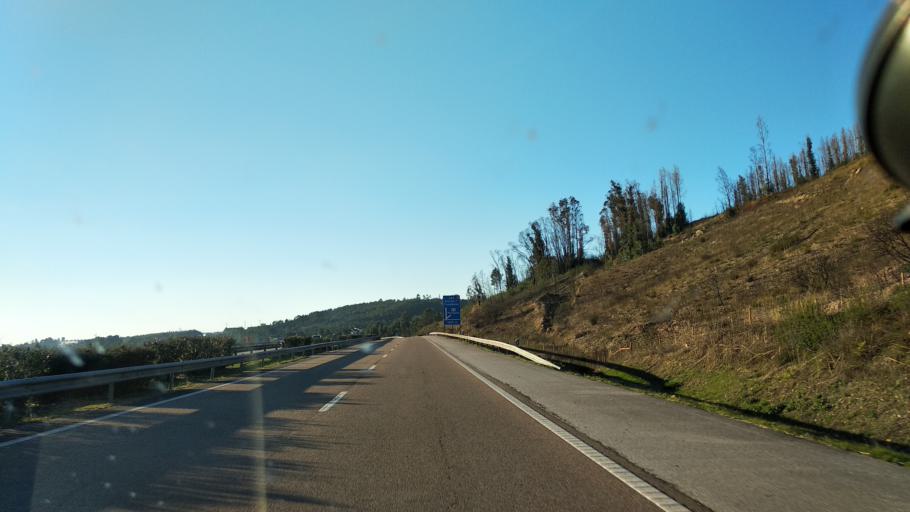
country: PT
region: Santarem
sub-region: Abrantes
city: Tramagal
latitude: 39.4859
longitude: -8.2585
